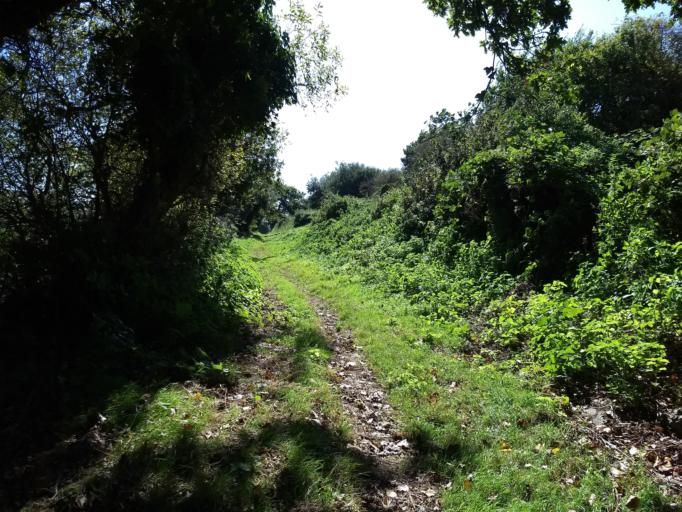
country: GB
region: England
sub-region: Isle of Wight
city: Niton
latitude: 50.6339
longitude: -1.2763
